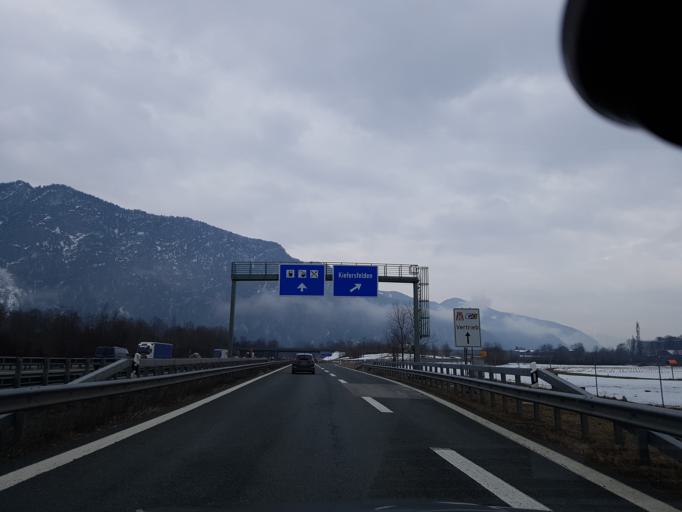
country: DE
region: Bavaria
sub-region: Upper Bavaria
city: Kiefersfelden
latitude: 47.6217
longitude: 12.2018
